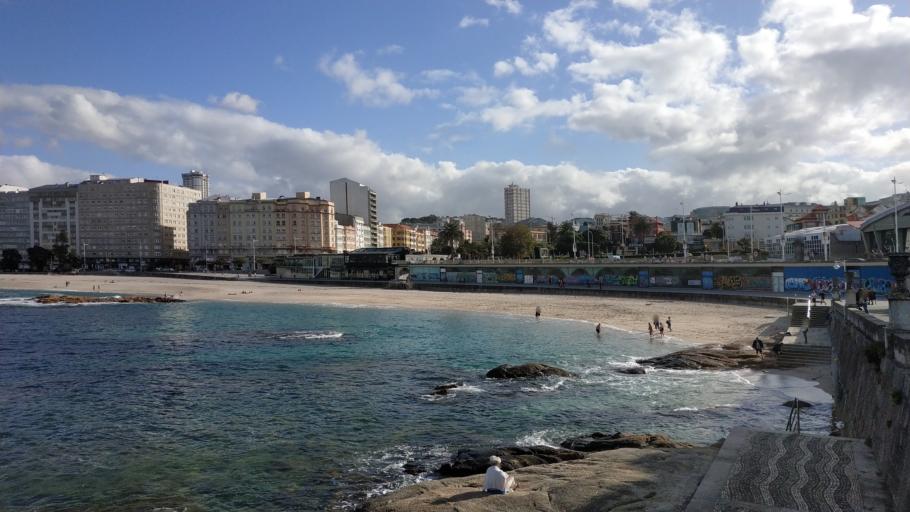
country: ES
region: Galicia
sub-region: Provincia da Coruna
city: A Coruna
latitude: 43.3704
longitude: -8.4144
